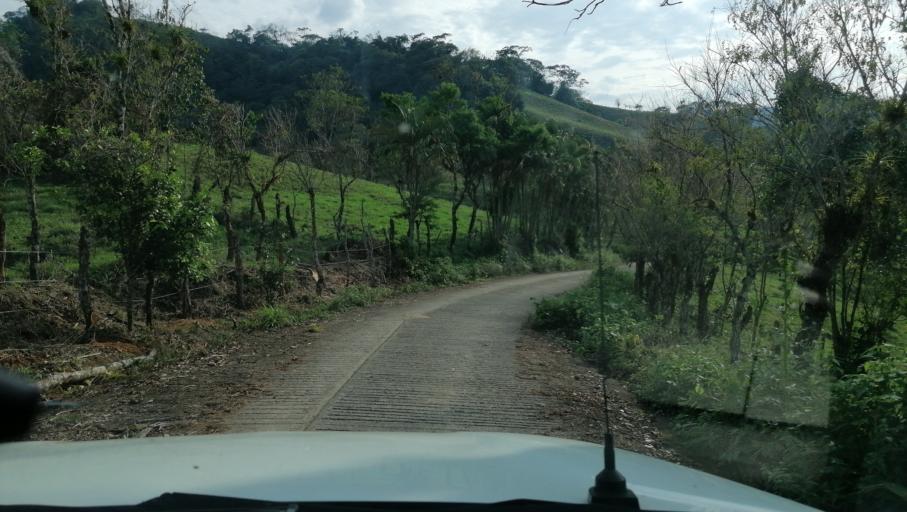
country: MX
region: Chiapas
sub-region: Juarez
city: El Triunfo 1ra. Seccion (Cardona)
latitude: 17.4851
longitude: -93.2397
